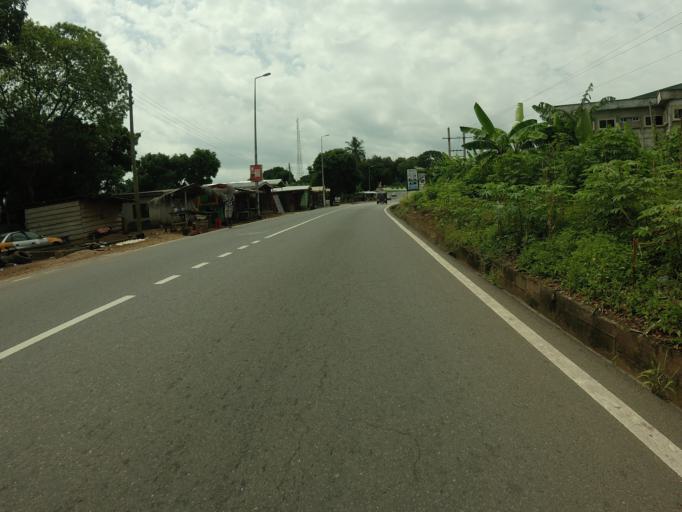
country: GH
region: Volta
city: Ho
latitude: 6.5973
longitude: 0.4725
